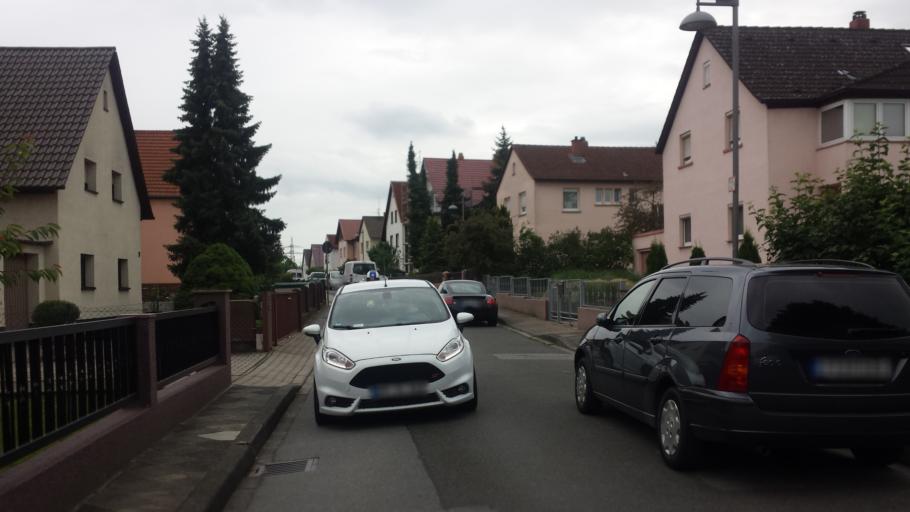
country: DE
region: Baden-Wuerttemberg
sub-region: Karlsruhe Region
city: Mannheim
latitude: 49.5202
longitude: 8.4918
